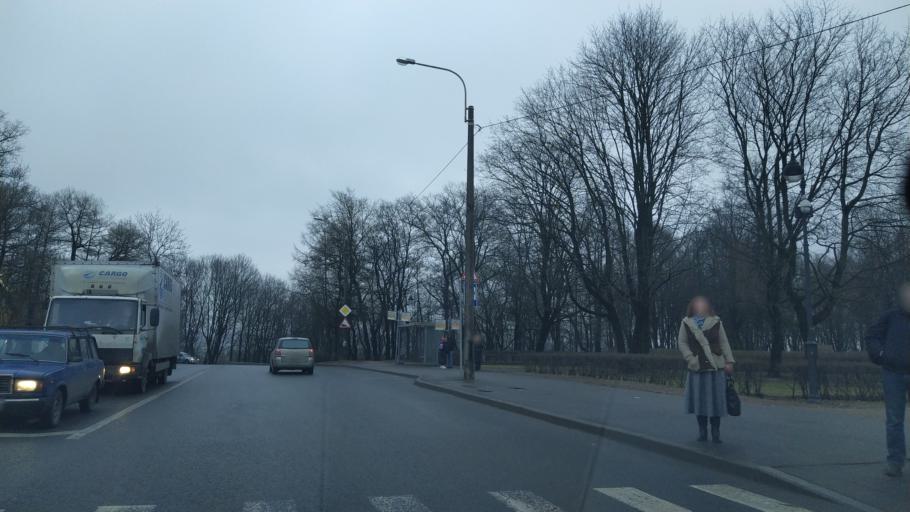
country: RU
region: St.-Petersburg
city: Krasnoye Selo
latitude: 59.7330
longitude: 30.0880
